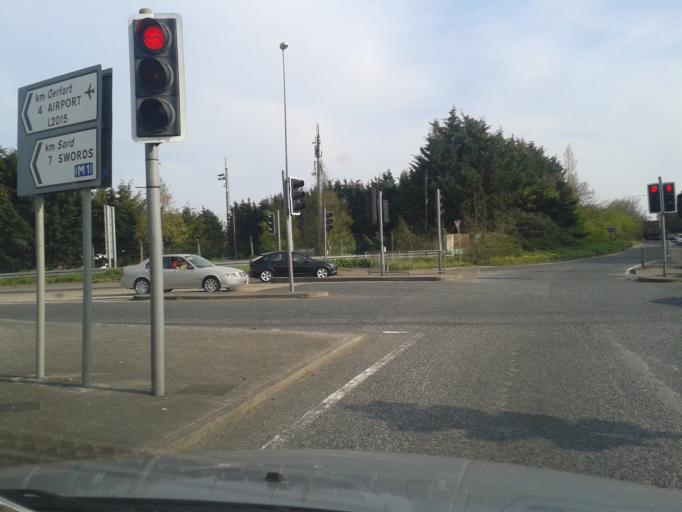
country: IE
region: Leinster
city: Ballymun
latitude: 53.4172
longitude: -6.2660
